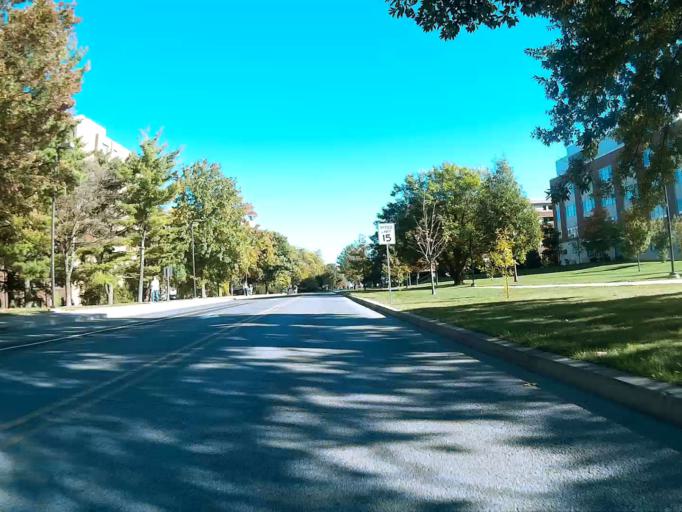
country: US
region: Pennsylvania
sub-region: Centre County
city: State College
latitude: 40.8058
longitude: -77.8644
